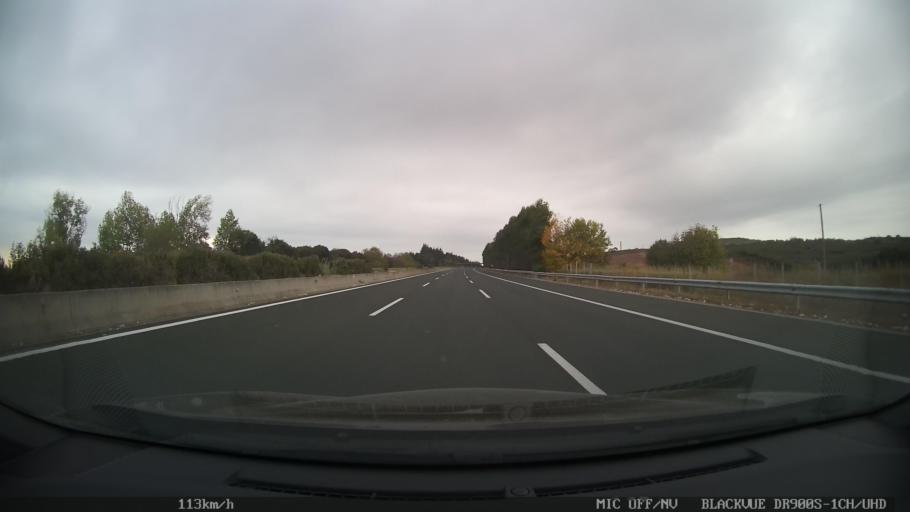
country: GR
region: Central Macedonia
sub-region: Nomos Pierias
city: Kitros
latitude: 40.3857
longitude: 22.6059
